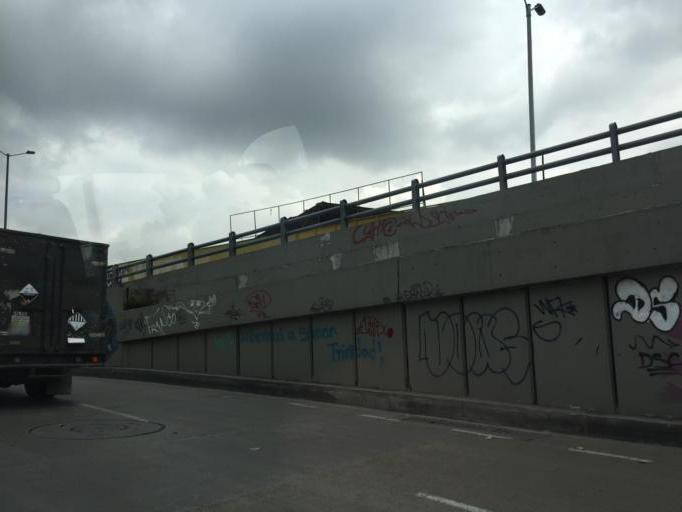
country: CO
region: Bogota D.C.
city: Bogota
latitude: 4.6251
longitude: -74.0795
